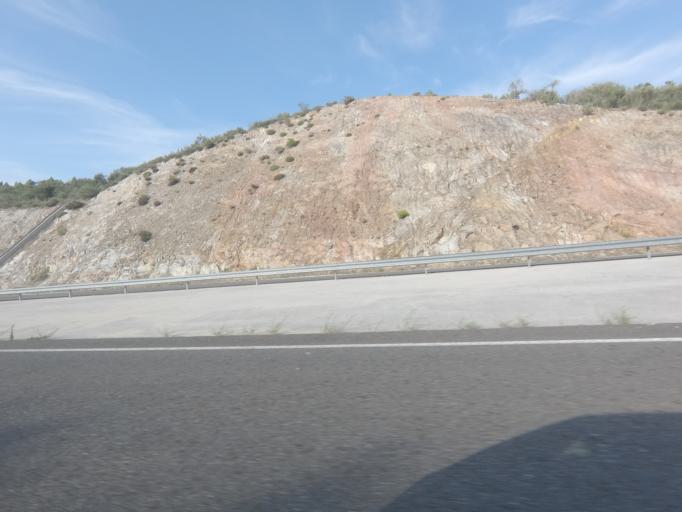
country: ES
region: Galicia
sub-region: Provincia de Ourense
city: Oimbra
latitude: 41.8583
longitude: -7.4248
